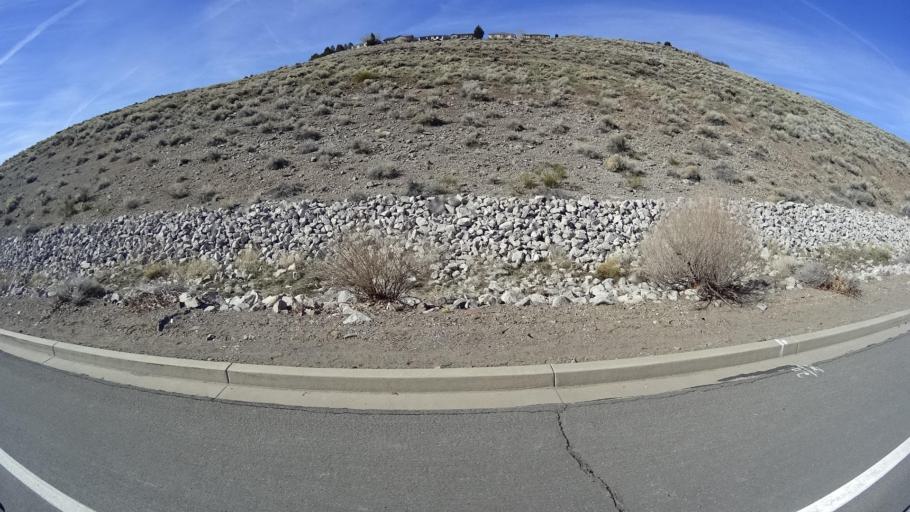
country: US
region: Nevada
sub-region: Washoe County
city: Sparks
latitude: 39.5736
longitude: -119.6953
